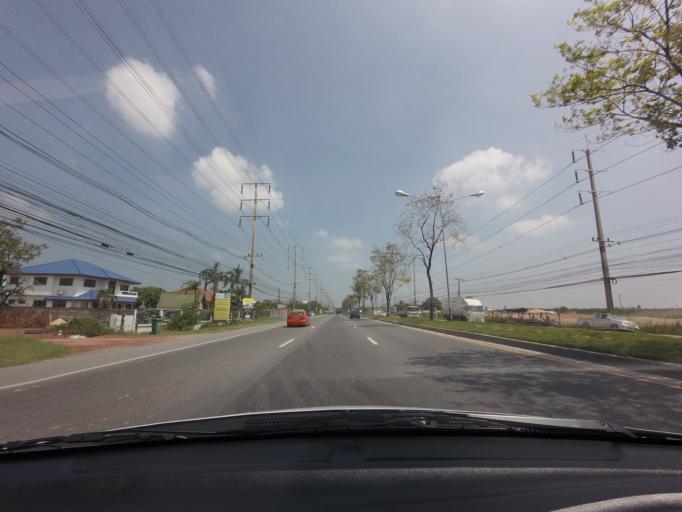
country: TH
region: Chachoengsao
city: Bang Pakong
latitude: 13.5822
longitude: 101.0081
